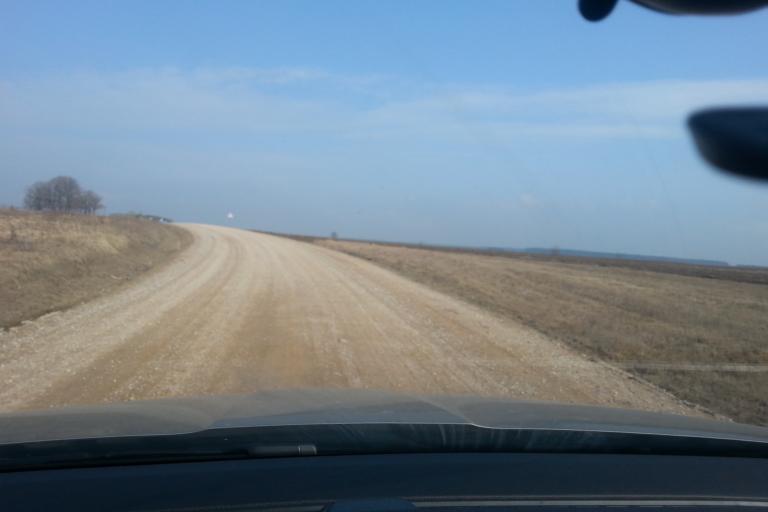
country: LT
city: Trakai
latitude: 54.5833
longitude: 24.9760
